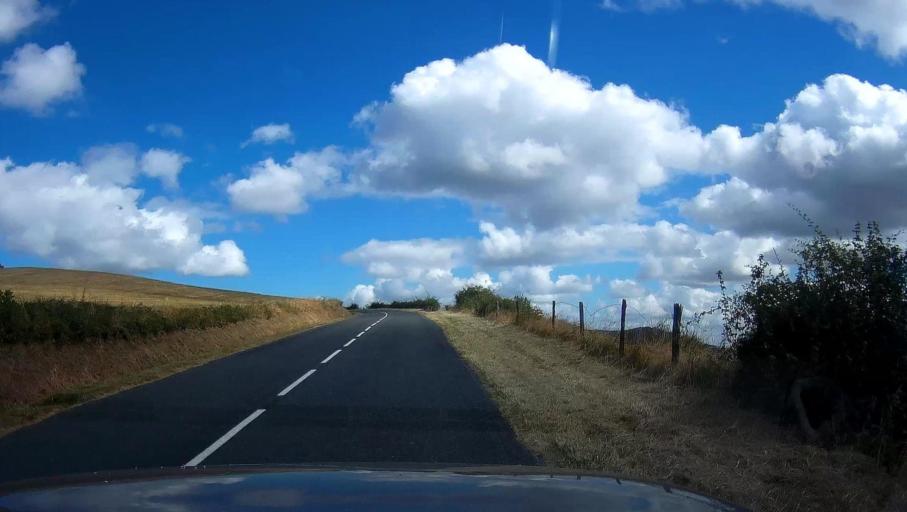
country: FR
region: Rhone-Alpes
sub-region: Departement du Rhone
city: Cogny
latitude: 45.9812
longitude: 4.5821
